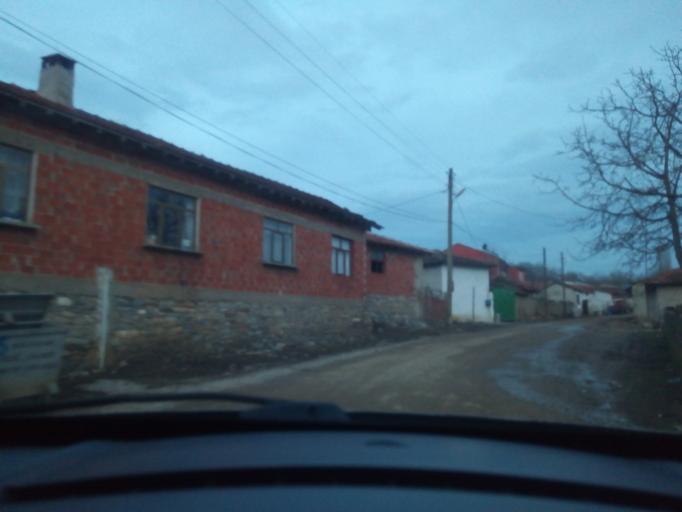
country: TR
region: Balikesir
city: Omerkoy
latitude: 39.9105
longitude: 28.0376
